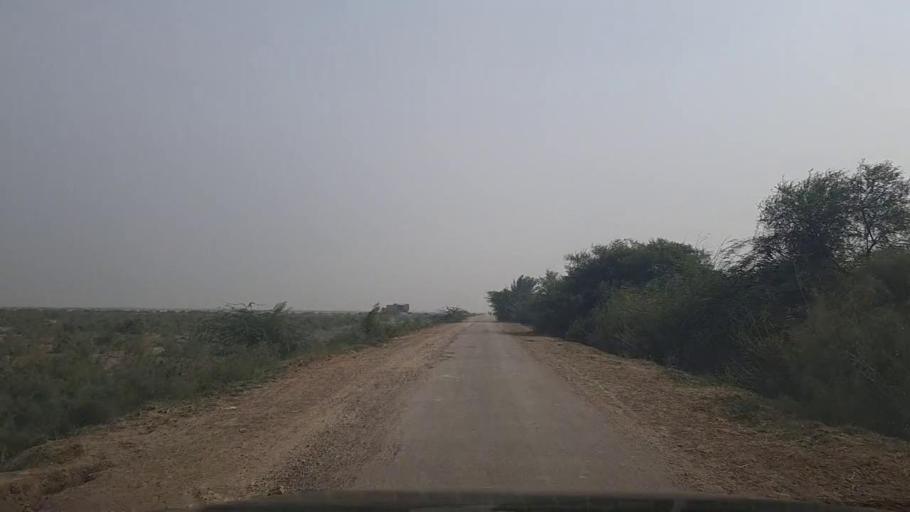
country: PK
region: Sindh
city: Mirpur Sakro
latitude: 24.4702
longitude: 67.6757
